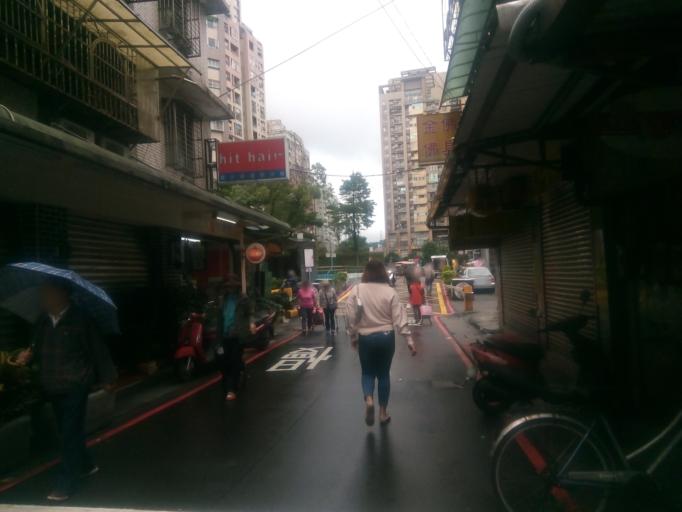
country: TW
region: Taiwan
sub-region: Keelung
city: Keelung
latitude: 25.0716
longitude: 121.6624
